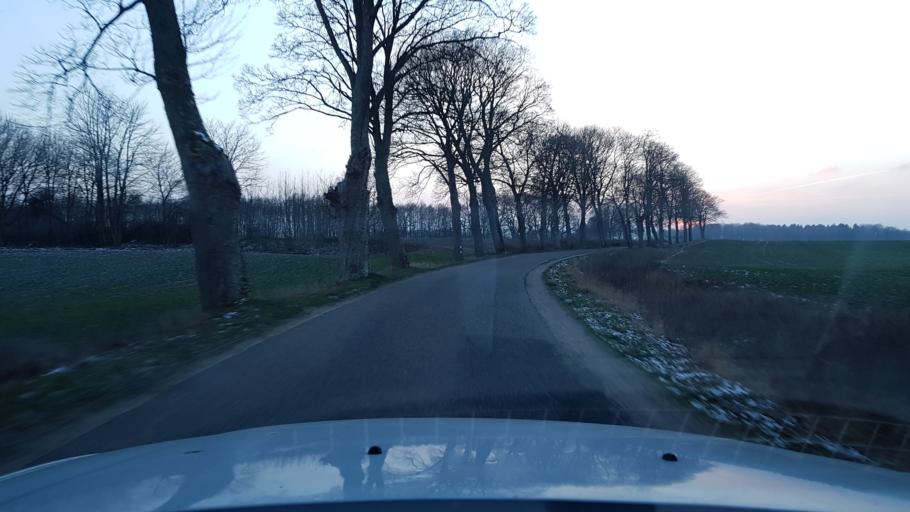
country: PL
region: West Pomeranian Voivodeship
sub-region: Powiat bialogardzki
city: Karlino
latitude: 54.0217
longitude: 15.8554
